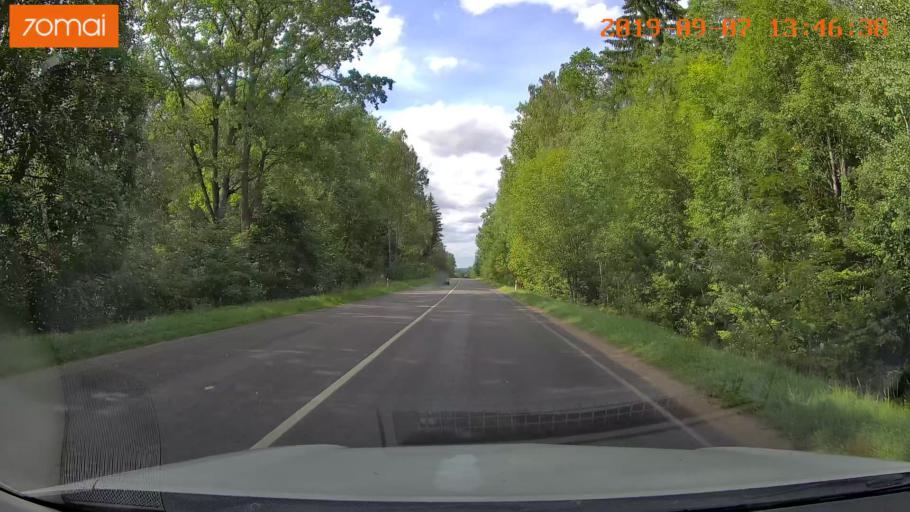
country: LT
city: Baltoji Voke
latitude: 54.5920
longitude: 25.2294
